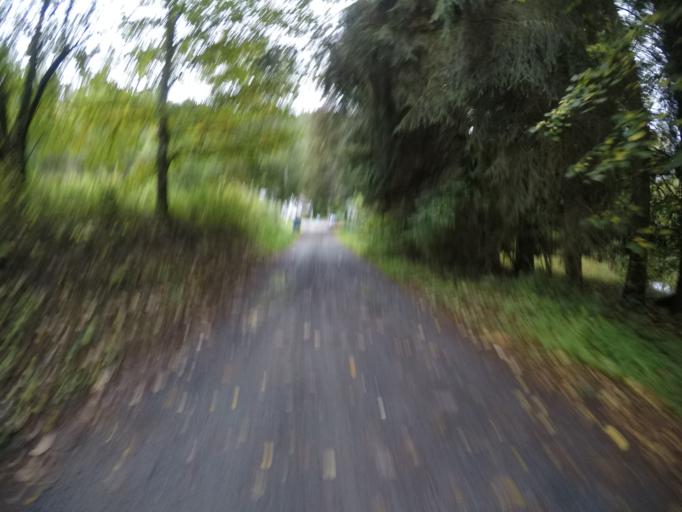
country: BE
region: Wallonia
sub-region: Province du Luxembourg
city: Fauvillers
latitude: 49.8549
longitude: 5.7000
